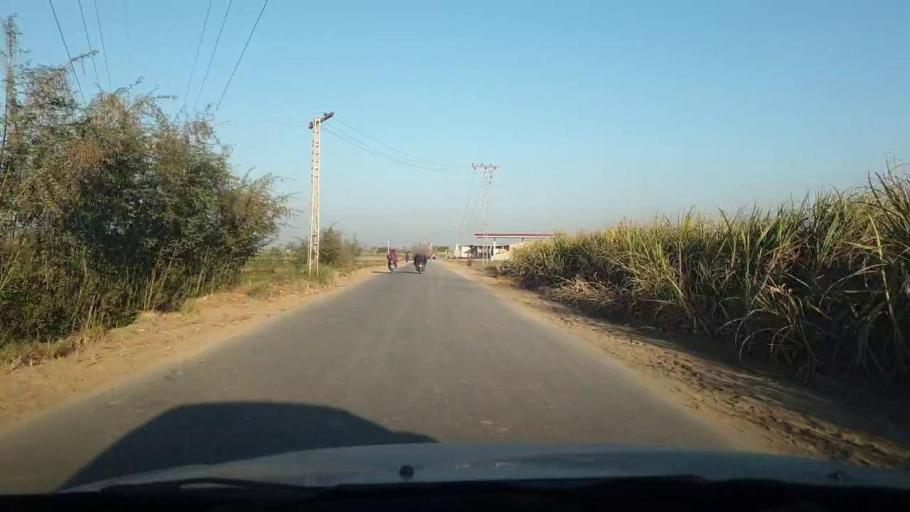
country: PK
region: Sindh
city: Ghotki
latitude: 27.9980
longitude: 69.2816
